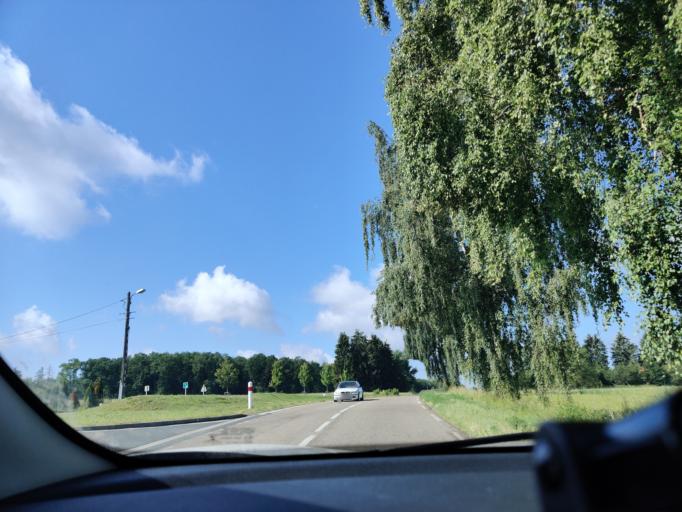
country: FR
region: Lorraine
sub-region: Departement de la Moselle
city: Sarreinsming
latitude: 49.1314
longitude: 7.1150
